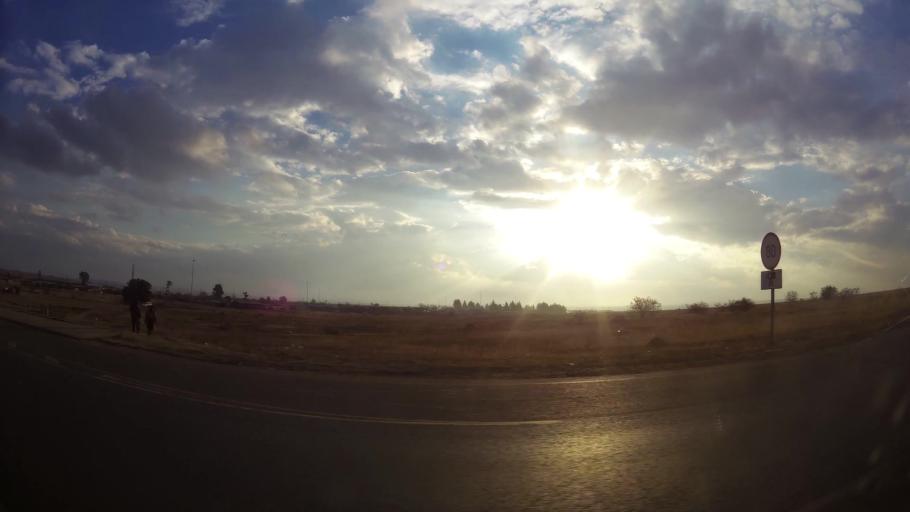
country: ZA
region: Gauteng
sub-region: Sedibeng District Municipality
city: Vanderbijlpark
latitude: -26.6012
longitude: 27.8183
